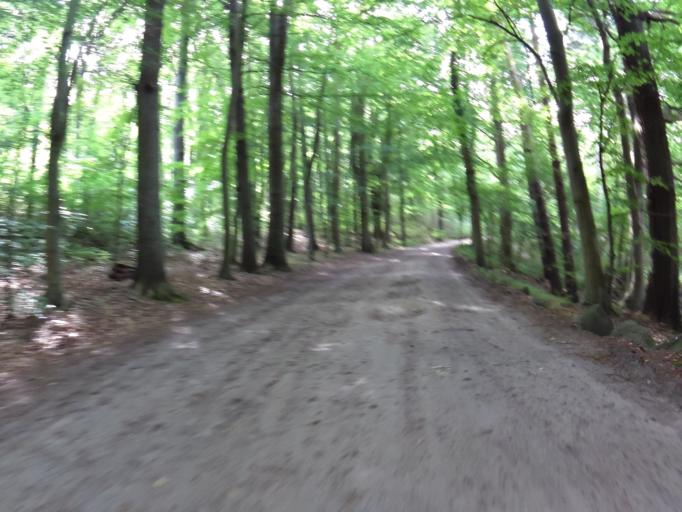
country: DE
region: Mecklenburg-Vorpommern
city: Seebad Bansin
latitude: 53.9656
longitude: 14.1077
